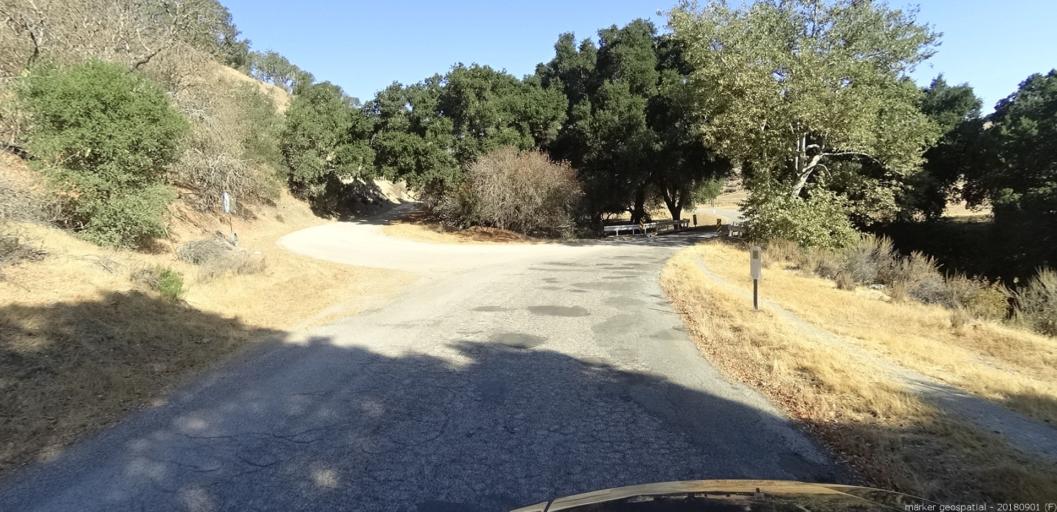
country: US
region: California
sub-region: Monterey County
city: Greenfield
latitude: 36.2376
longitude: -121.2850
